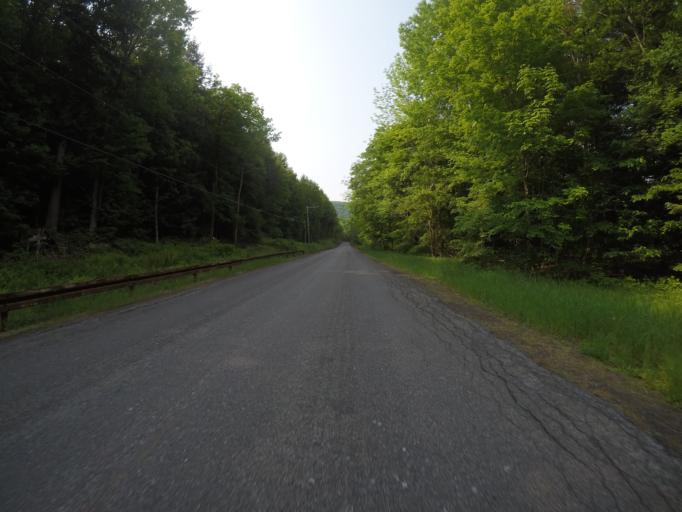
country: US
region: New York
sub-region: Sullivan County
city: Livingston Manor
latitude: 42.0945
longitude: -74.7914
